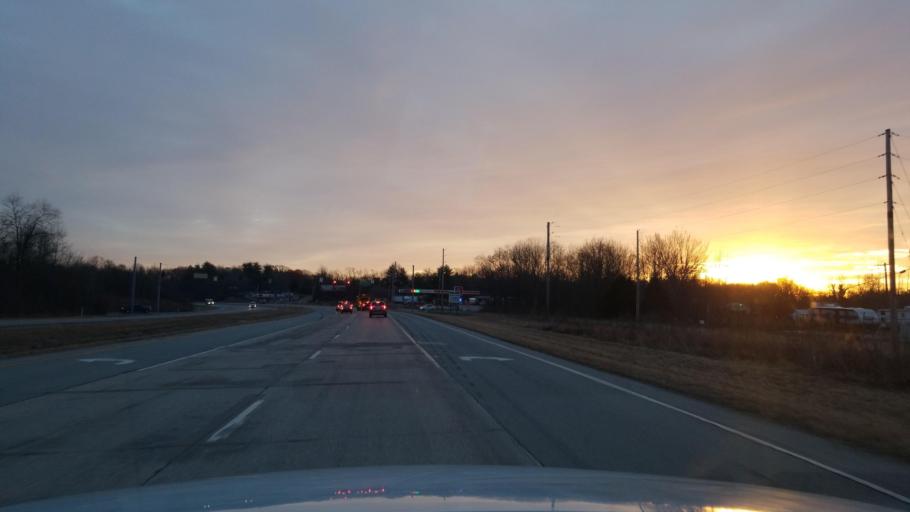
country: US
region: Indiana
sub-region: Vanderburgh County
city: Evansville
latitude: 37.9423
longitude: -87.7208
